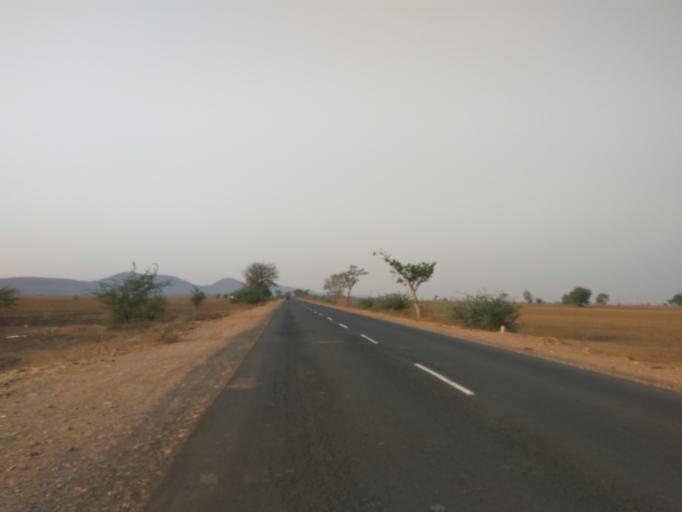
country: IN
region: Andhra Pradesh
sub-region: Prakasam
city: Cumbum
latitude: 15.6245
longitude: 79.1351
